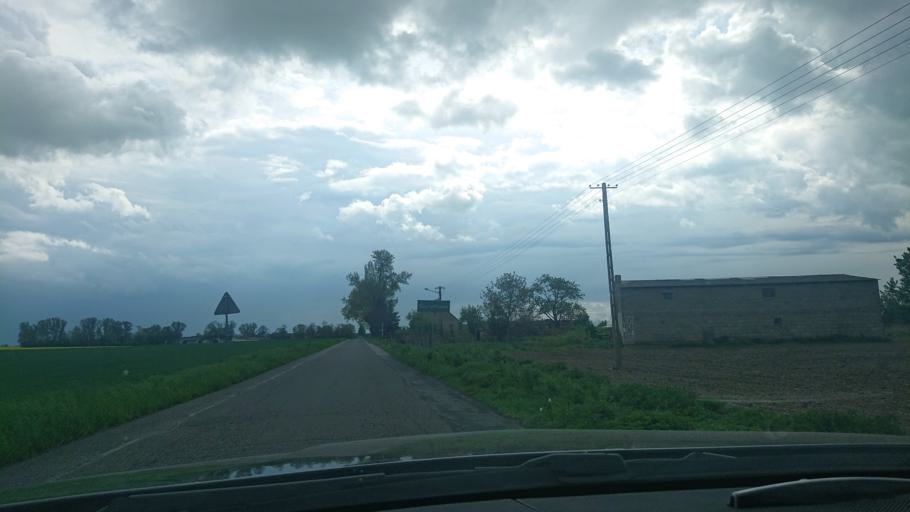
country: PL
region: Greater Poland Voivodeship
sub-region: Powiat gnieznienski
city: Niechanowo
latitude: 52.4755
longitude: 17.6369
